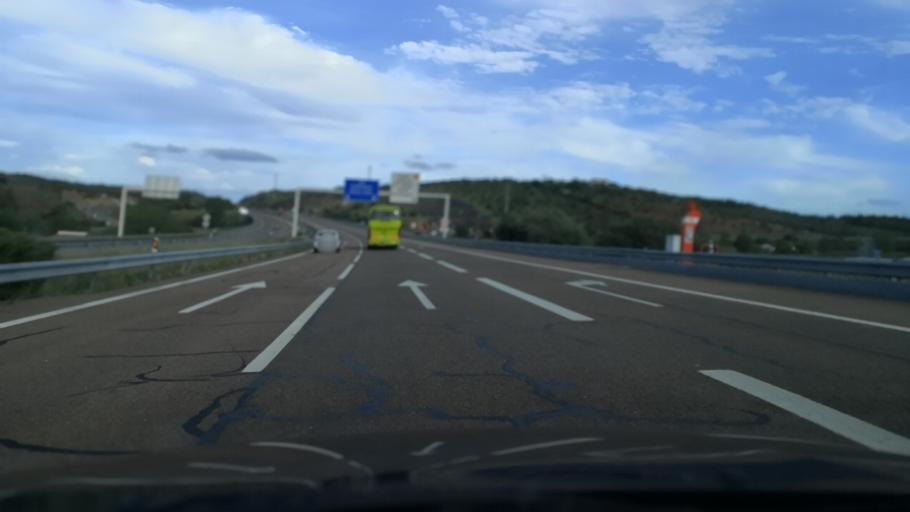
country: PT
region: Portalegre
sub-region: Elvas
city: Elvas
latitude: 38.9043
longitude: -7.1546
